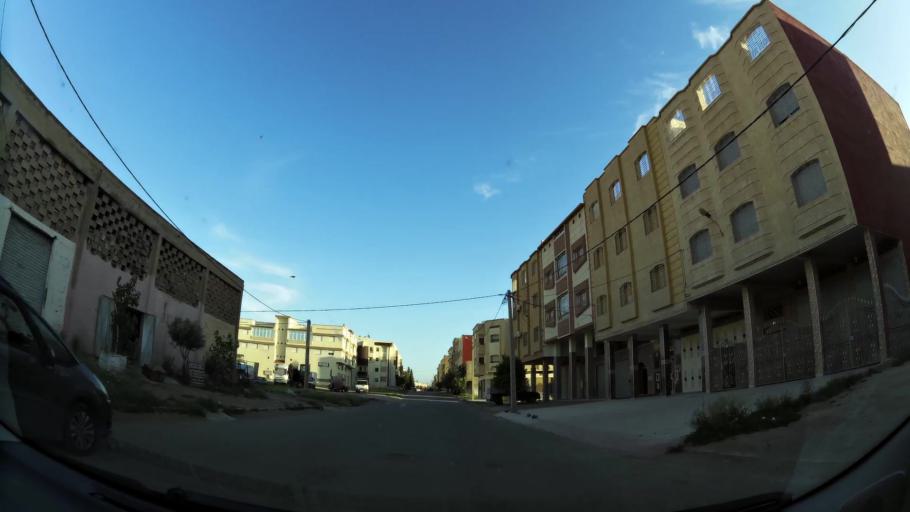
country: MA
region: Oriental
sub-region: Oujda-Angad
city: Oujda
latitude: 34.7005
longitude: -1.9163
